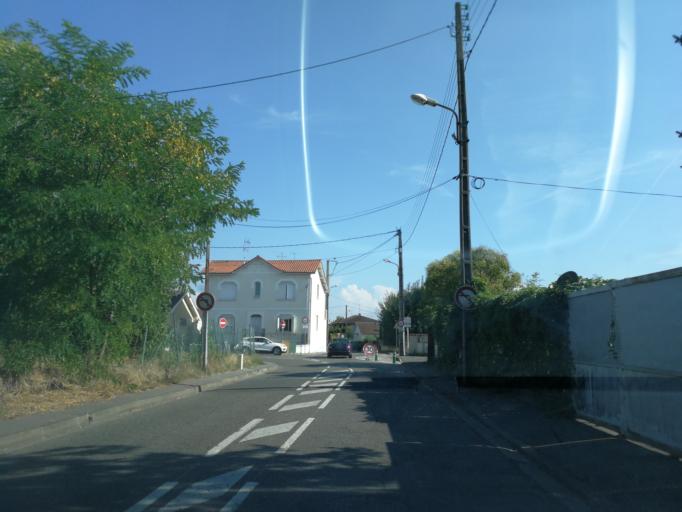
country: FR
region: Midi-Pyrenees
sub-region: Departement de la Haute-Garonne
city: Toulouse
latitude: 43.6285
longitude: 1.4248
